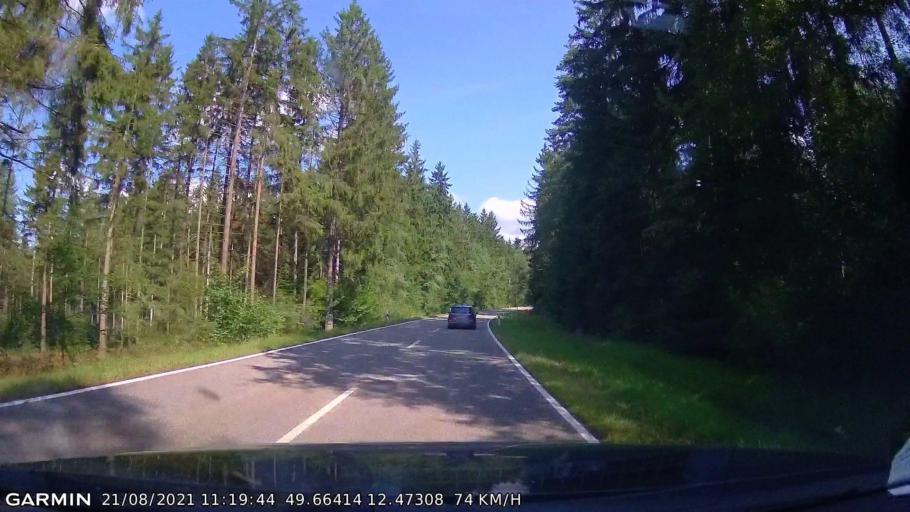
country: DE
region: Bavaria
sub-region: Upper Palatinate
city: Waidhaus
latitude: 49.6642
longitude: 12.4731
